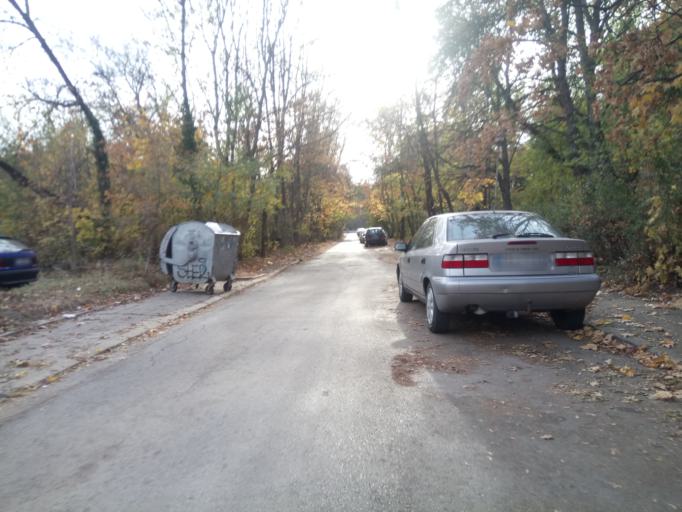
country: BG
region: Sofia-Capital
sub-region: Stolichna Obshtina
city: Sofia
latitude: 42.6826
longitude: 23.3529
